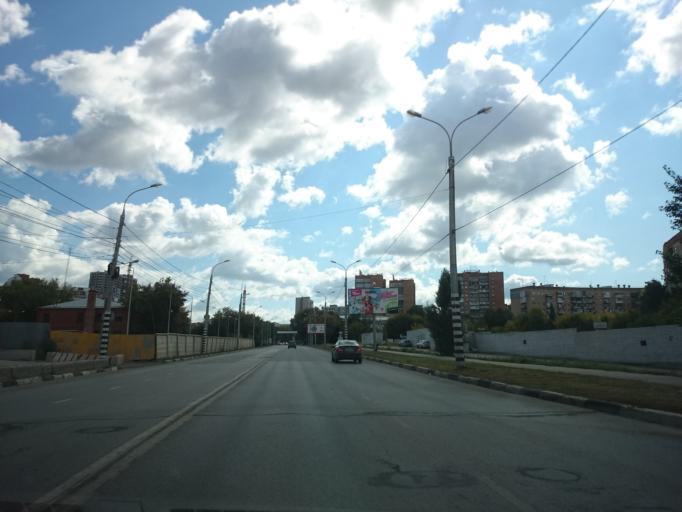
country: RU
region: Samara
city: Samara
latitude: 53.2153
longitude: 50.1381
